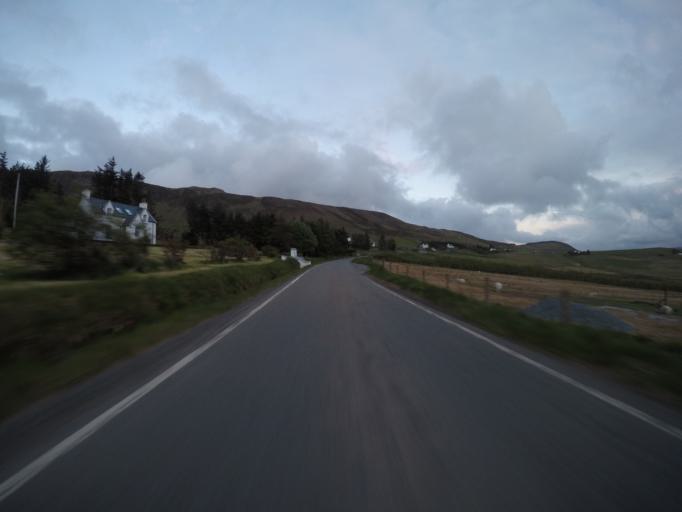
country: GB
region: Scotland
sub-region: Highland
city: Portree
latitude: 57.6166
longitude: -6.3717
